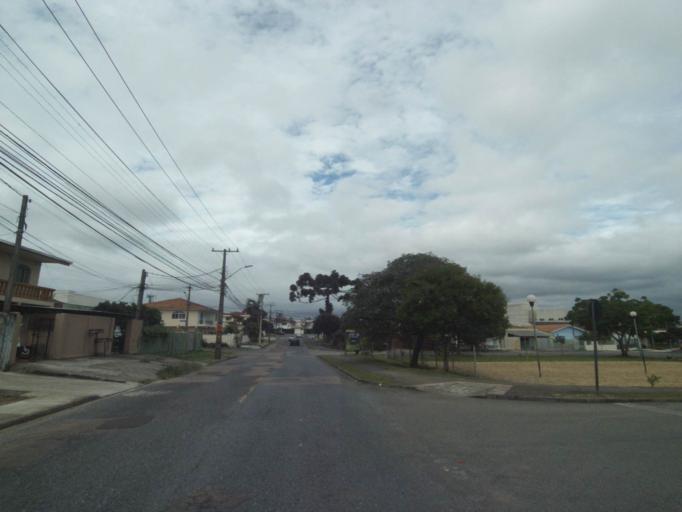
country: BR
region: Parana
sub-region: Curitiba
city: Curitiba
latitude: -25.4970
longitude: -49.2883
